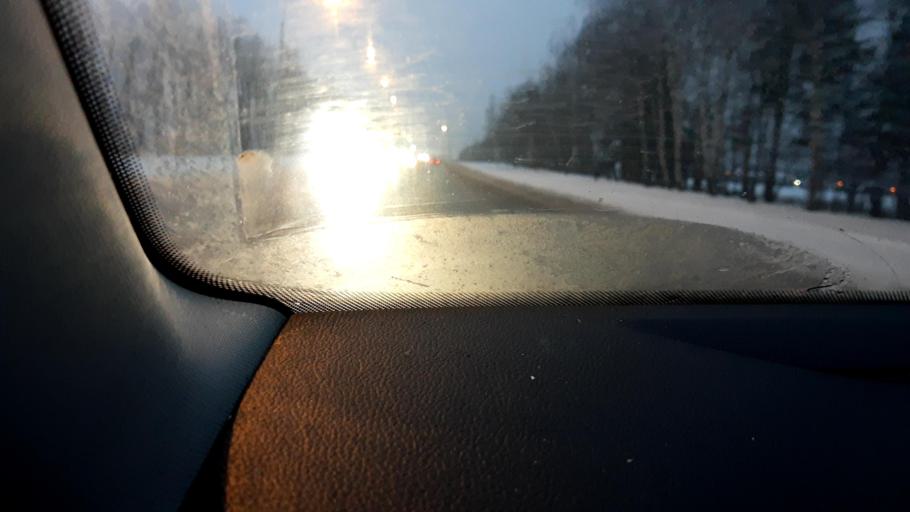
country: RU
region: Moskovskaya
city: Troitsk
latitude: 55.3322
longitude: 37.1674
